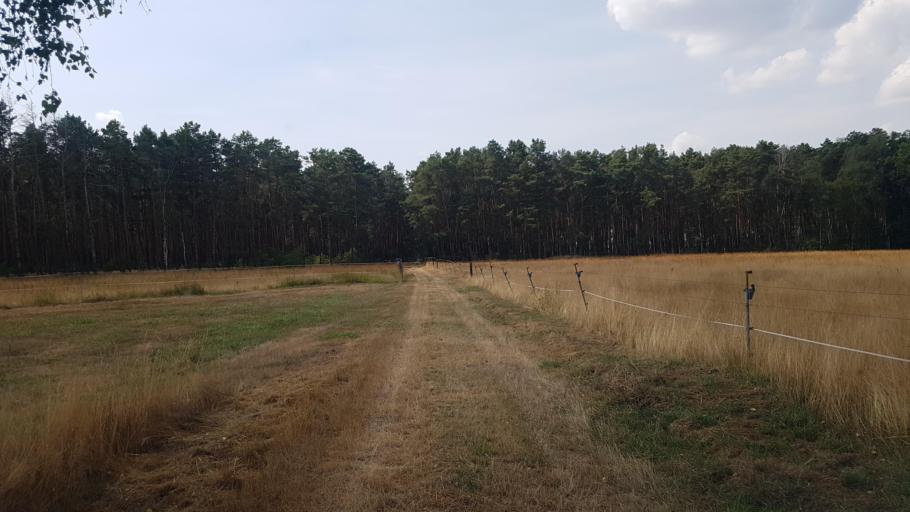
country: DE
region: Brandenburg
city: Finsterwalde
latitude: 51.6554
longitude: 13.7466
